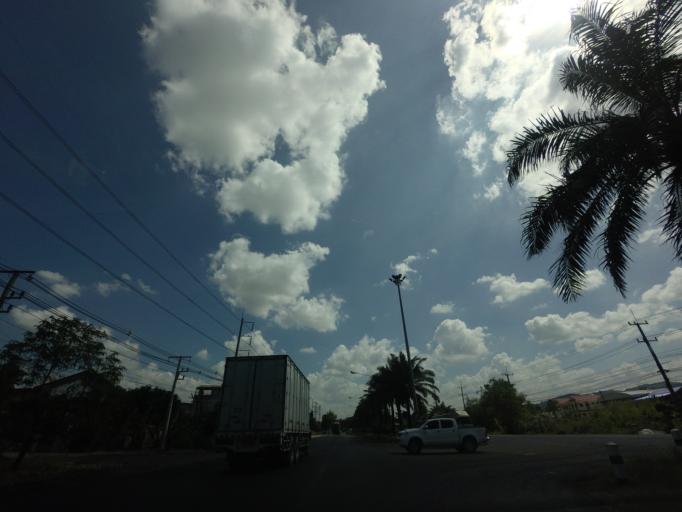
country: TH
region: Chon Buri
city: Ban Bueng
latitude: 13.3066
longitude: 101.1093
